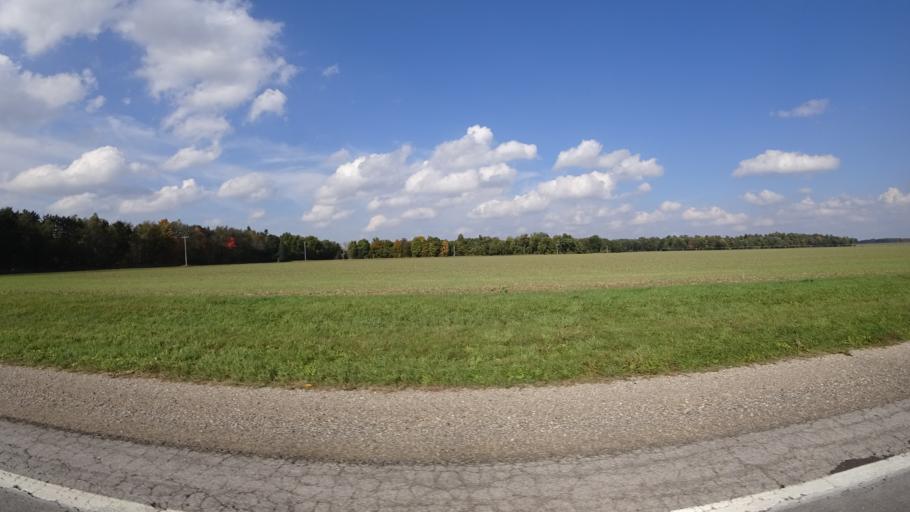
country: US
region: Michigan
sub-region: Saint Joseph County
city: Colon
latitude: 42.0102
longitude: -85.3799
